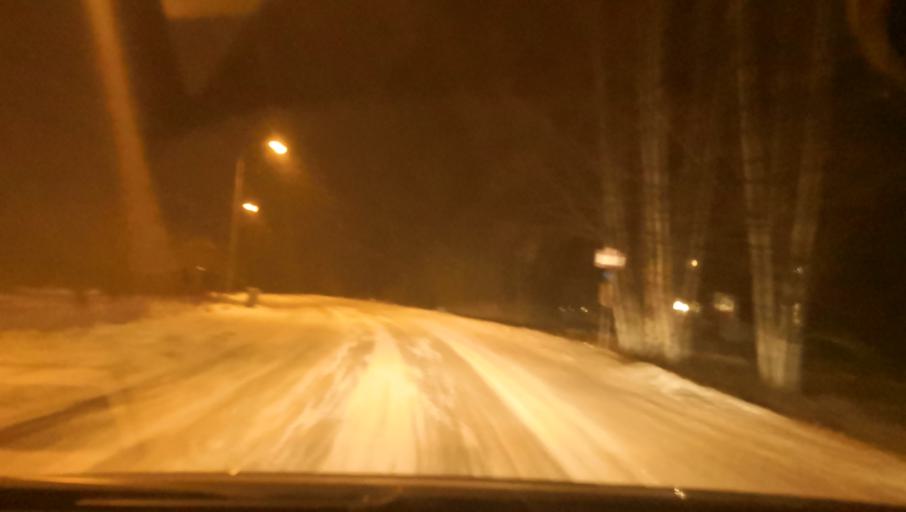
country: SE
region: Uppsala
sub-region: Heby Kommun
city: Tarnsjo
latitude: 60.1441
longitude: 16.9114
